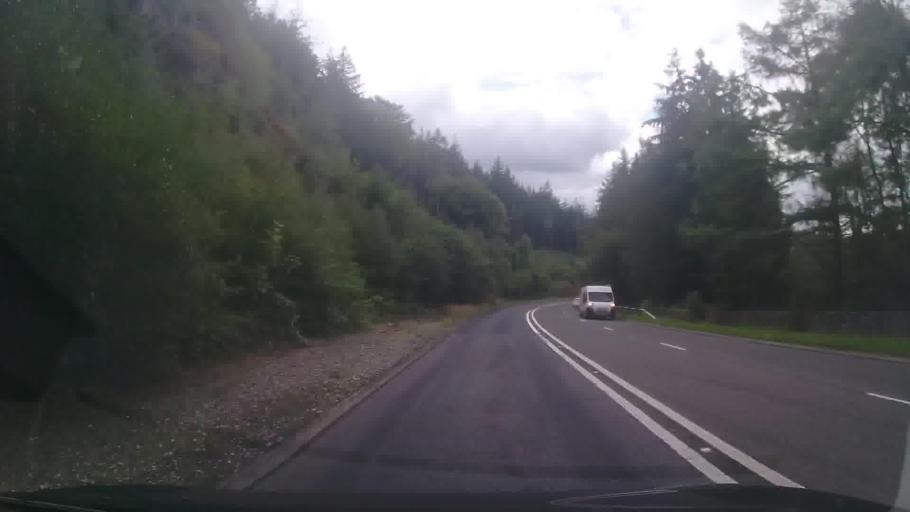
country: GB
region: Wales
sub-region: Gwynedd
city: Dolgellau
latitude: 52.7485
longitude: -3.8534
